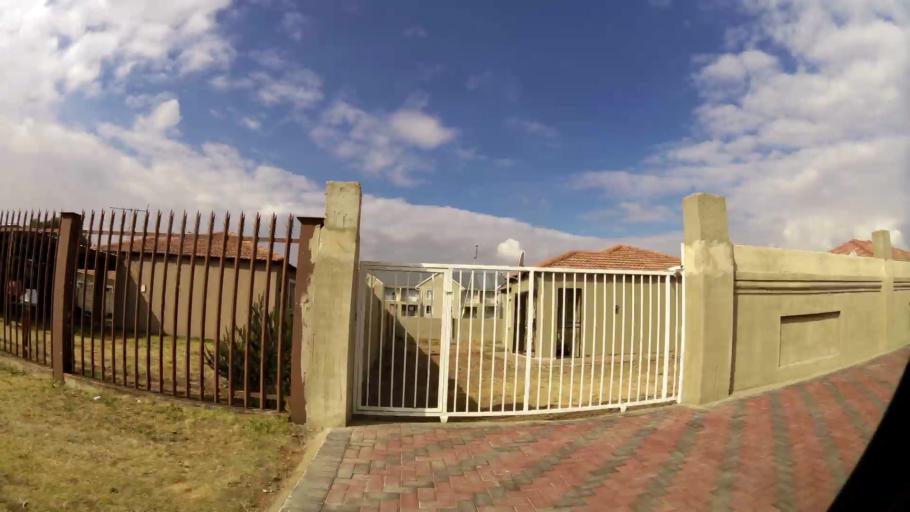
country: ZA
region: Gauteng
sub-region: Sedibeng District Municipality
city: Vanderbijlpark
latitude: -26.7175
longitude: 27.8850
